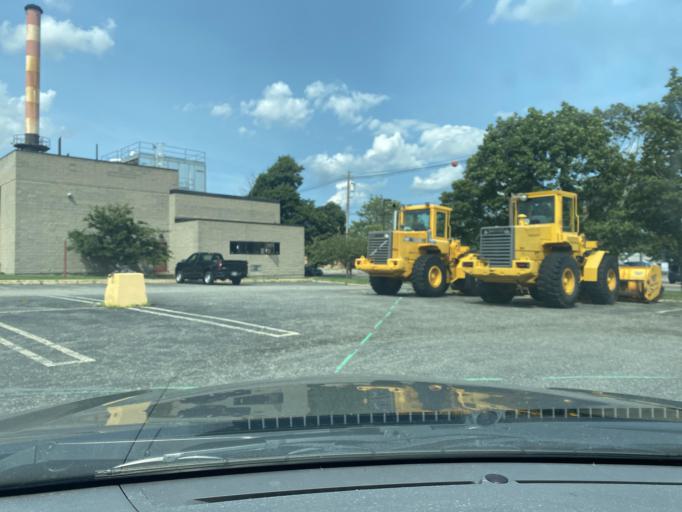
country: US
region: Massachusetts
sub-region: Norfolk County
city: Norwood
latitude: 42.1881
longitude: -71.2009
